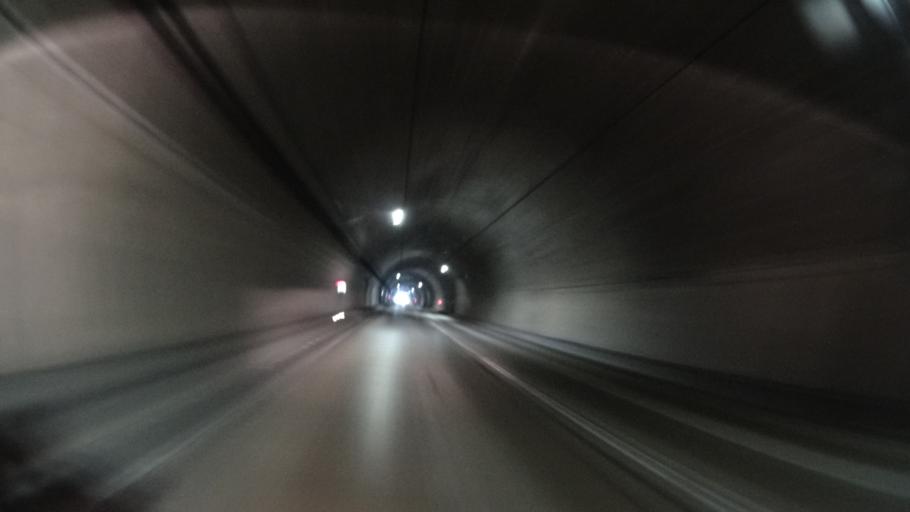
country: JP
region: Fukui
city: Maruoka
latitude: 36.1332
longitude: 136.3242
